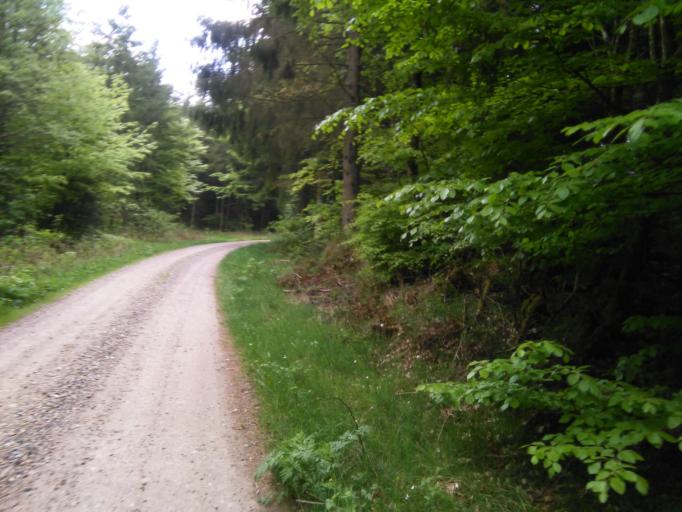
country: DK
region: Central Jutland
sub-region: Horsens Kommune
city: Braedstrup
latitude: 56.0495
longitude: 9.6126
